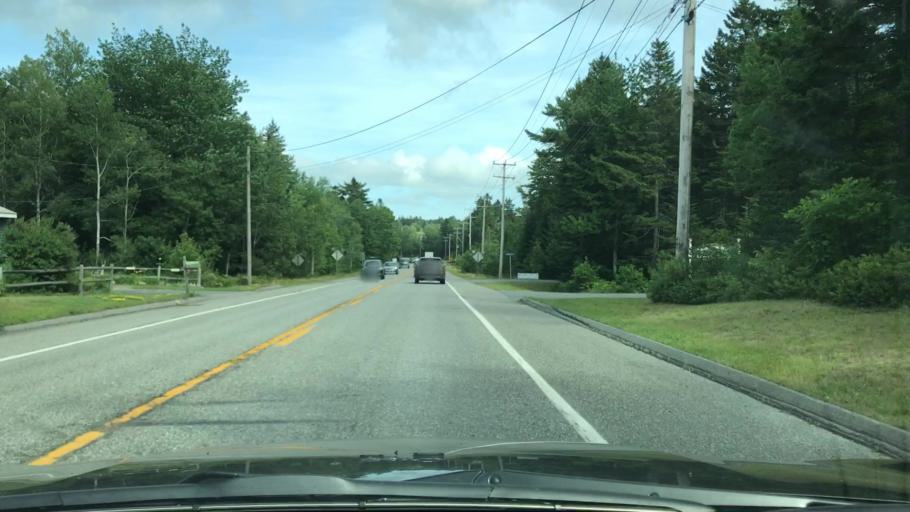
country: US
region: Maine
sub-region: Hancock County
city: Trenton
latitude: 44.4197
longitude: -68.3570
